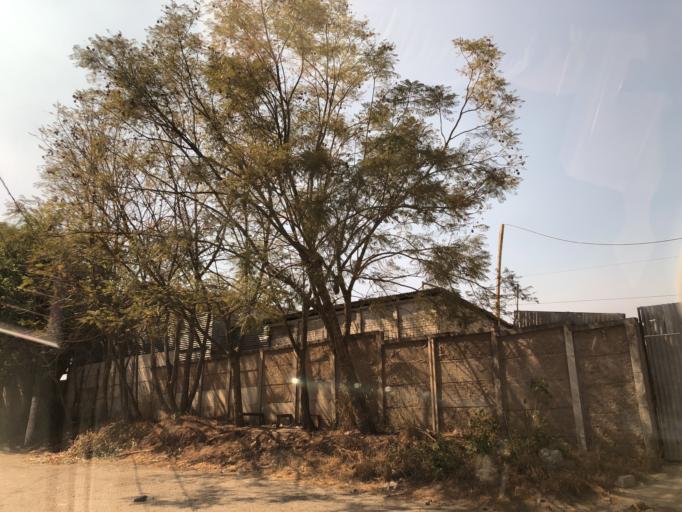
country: GT
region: Guatemala
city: Amatitlan
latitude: 14.4992
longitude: -90.5970
